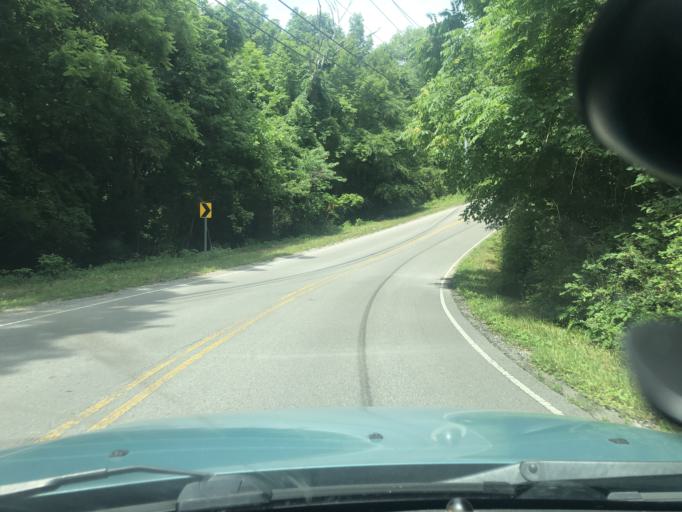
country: US
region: Tennessee
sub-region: Rutherford County
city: La Vergne
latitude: 36.1232
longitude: -86.6340
